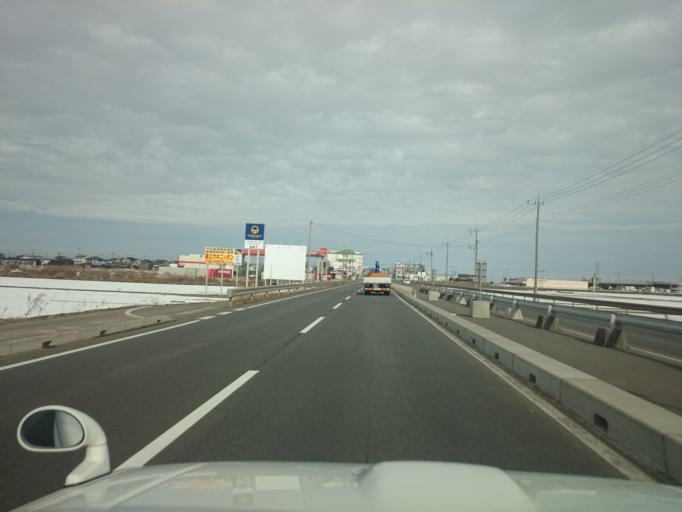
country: JP
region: Ibaraki
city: Ishige
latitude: 36.1020
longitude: 139.9847
